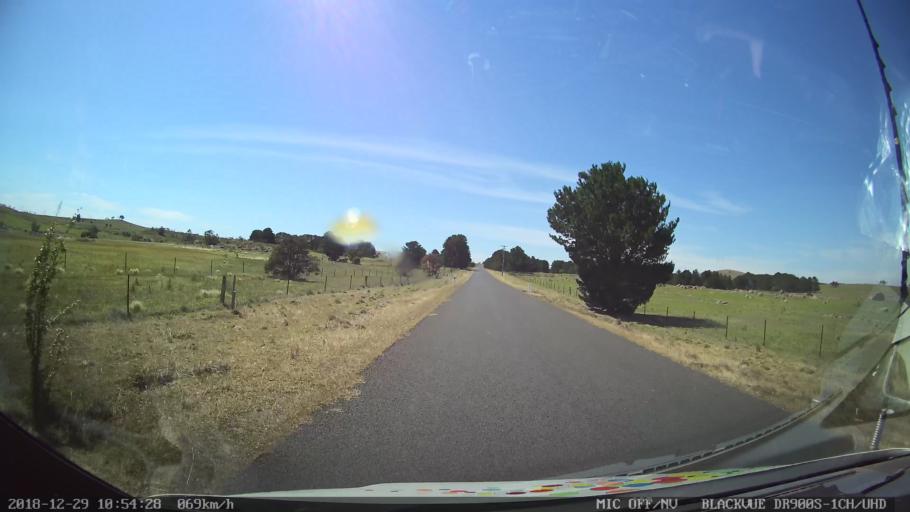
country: AU
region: New South Wales
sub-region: Palerang
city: Bungendore
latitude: -35.1149
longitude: 149.5271
